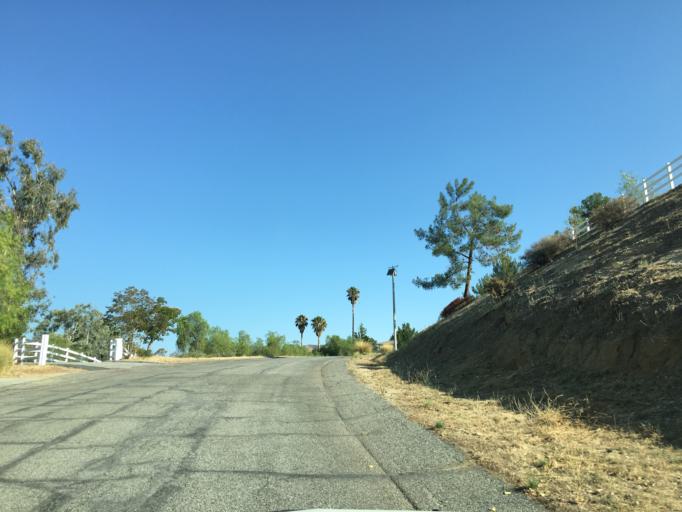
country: US
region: California
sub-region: Los Angeles County
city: Val Verde
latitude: 34.4690
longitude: -118.6654
